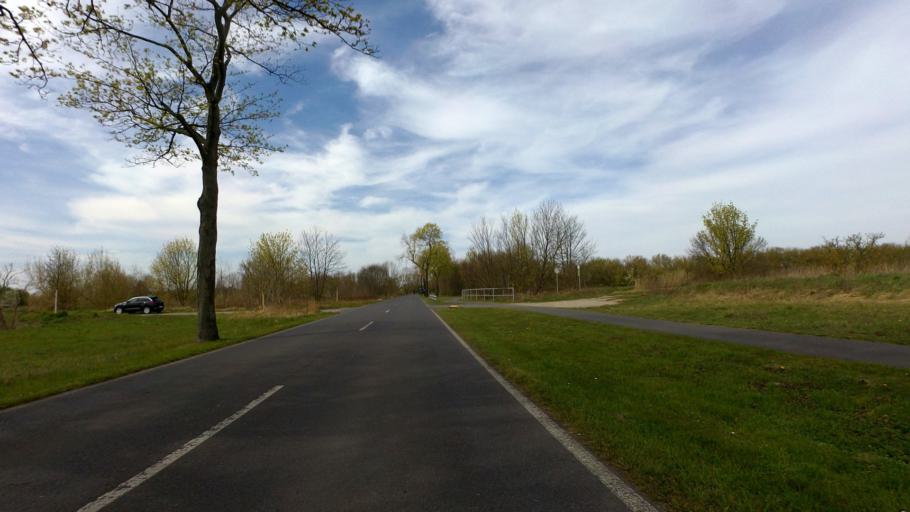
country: DE
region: Berlin
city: Gropiusstadt
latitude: 52.3748
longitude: 13.4576
